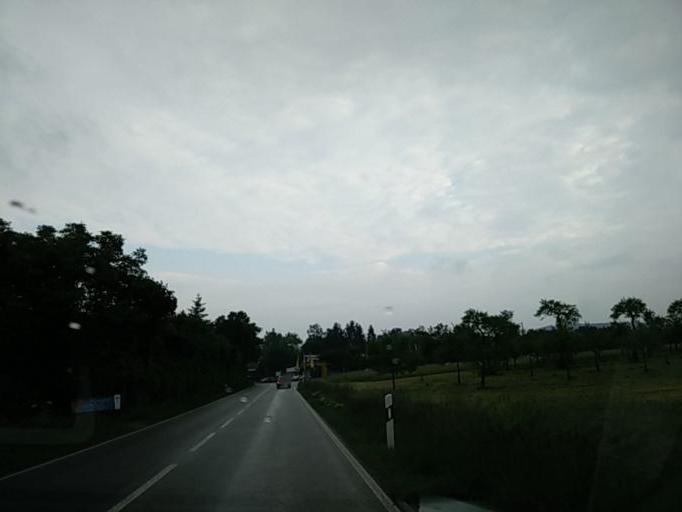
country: DE
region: Baden-Wuerttemberg
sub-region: Tuebingen Region
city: Rottenburg
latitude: 48.5448
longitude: 8.9666
